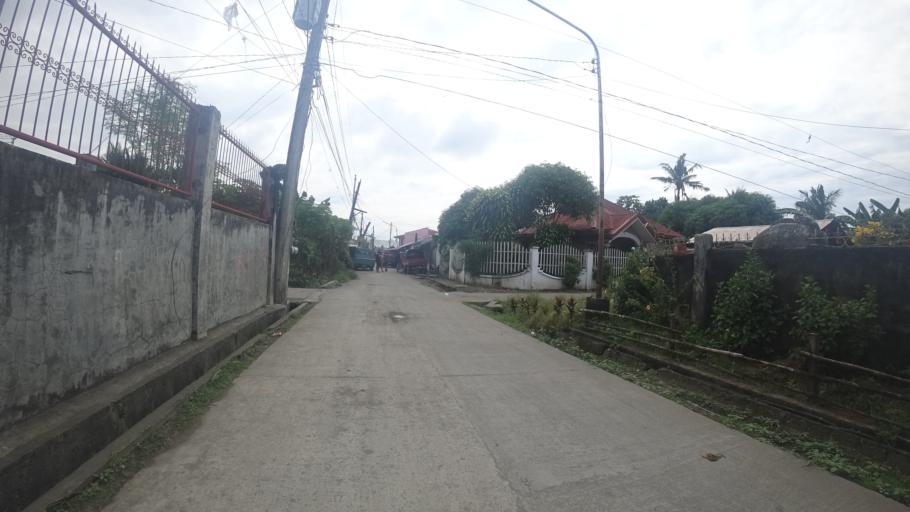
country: PH
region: Eastern Visayas
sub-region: Province of Leyte
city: Baras
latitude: 11.2061
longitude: 125.0119
